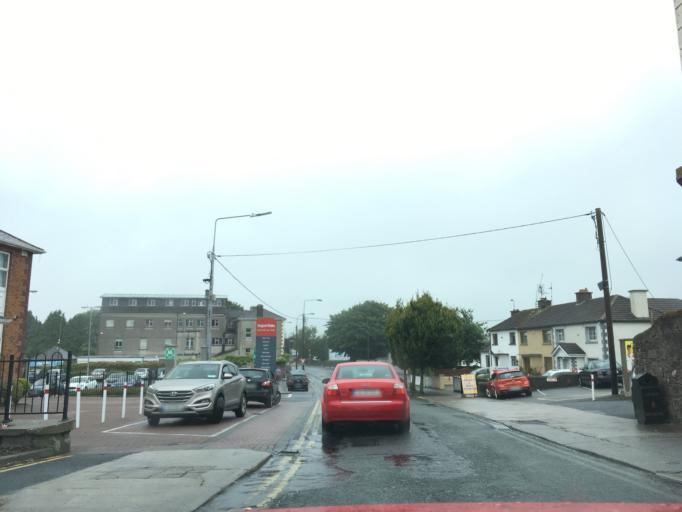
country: IE
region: Munster
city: Carrick-on-Suir
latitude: 52.3471
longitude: -7.4157
